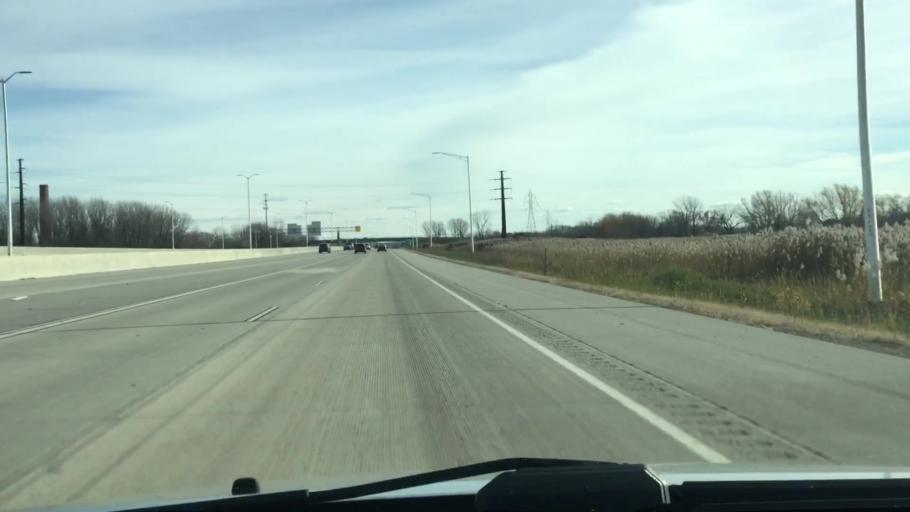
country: US
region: Wisconsin
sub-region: Brown County
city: Howard
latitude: 44.5561
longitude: -88.0477
